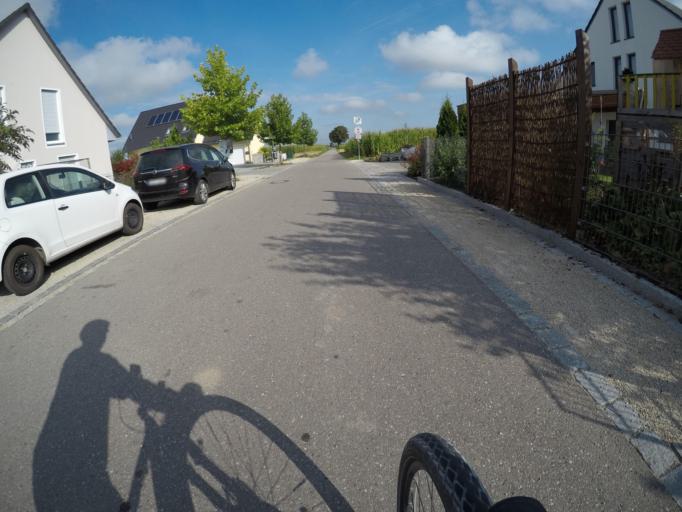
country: DE
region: Bavaria
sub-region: Swabia
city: Westendorf
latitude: 48.5771
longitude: 10.8372
